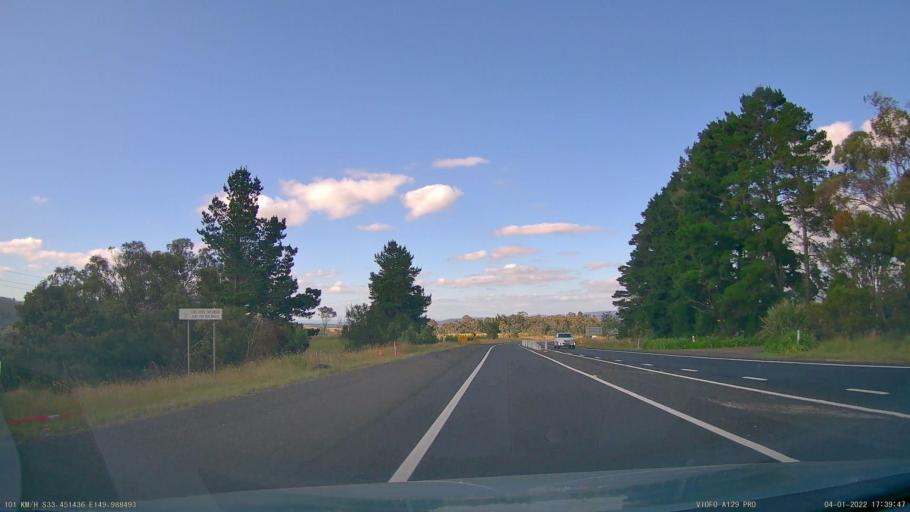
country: AU
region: New South Wales
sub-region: Lithgow
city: Portland
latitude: -33.4511
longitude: 149.9883
